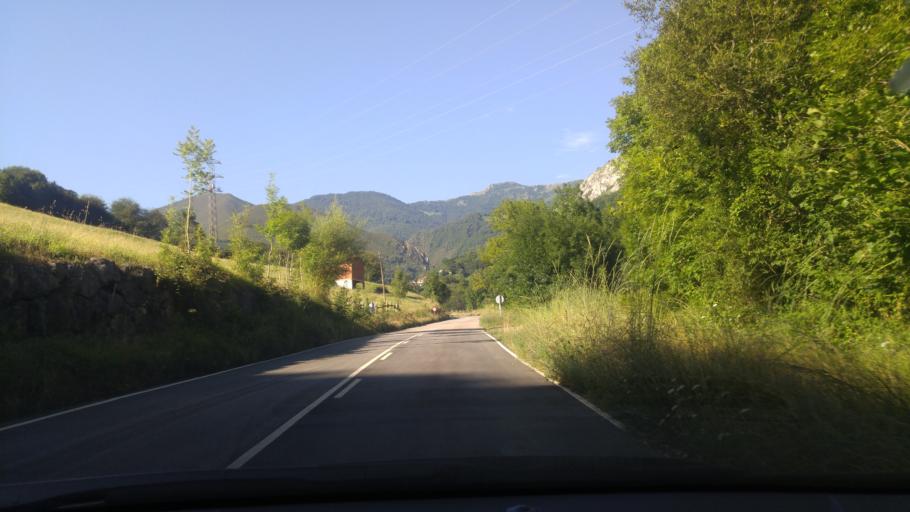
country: ES
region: Asturias
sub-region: Province of Asturias
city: Barzana
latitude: 43.1823
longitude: -5.9929
